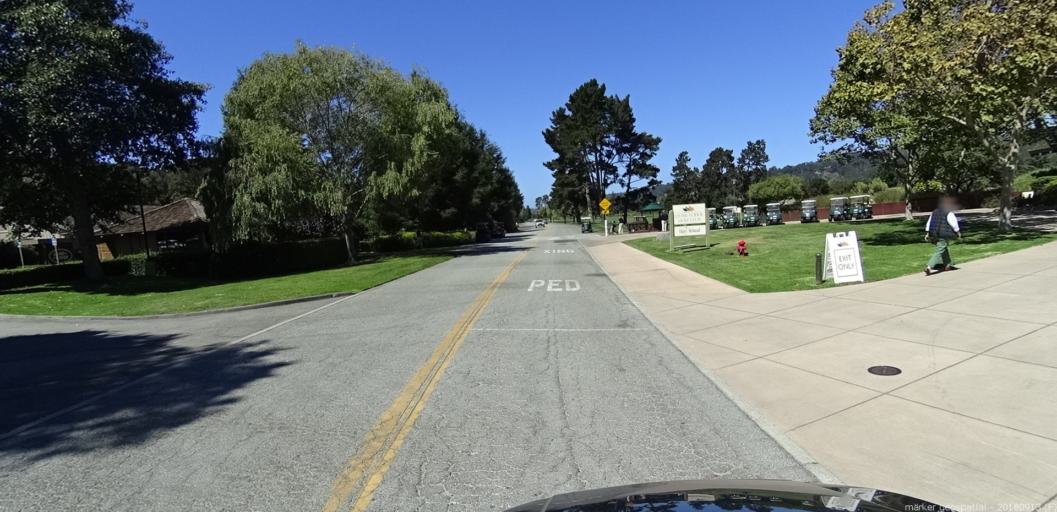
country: US
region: California
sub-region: Monterey County
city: Del Rey Oaks
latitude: 36.5304
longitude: -121.8593
